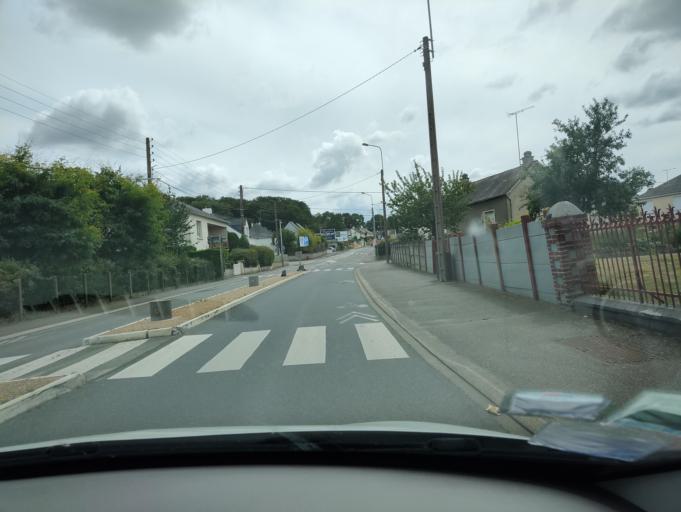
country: FR
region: Pays de la Loire
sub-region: Departement de la Loire-Atlantique
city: Chateaubriant
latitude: 47.7100
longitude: -1.3813
